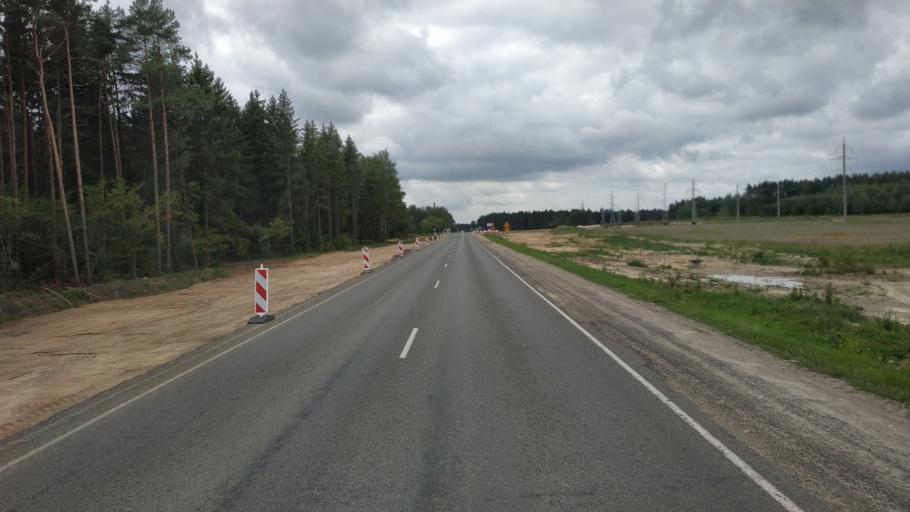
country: BY
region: Mogilev
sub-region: Mahilyowski Rayon
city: Veyno
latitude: 53.8743
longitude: 30.4374
